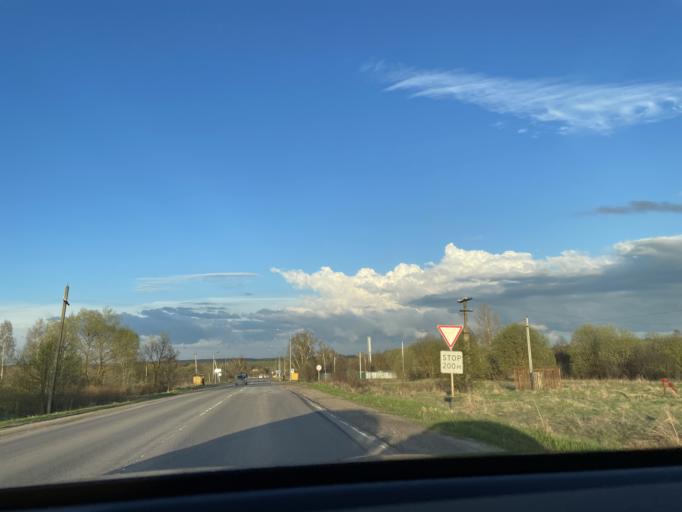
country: RU
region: Tula
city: Novogurovskiy
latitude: 54.5220
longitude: 37.4631
